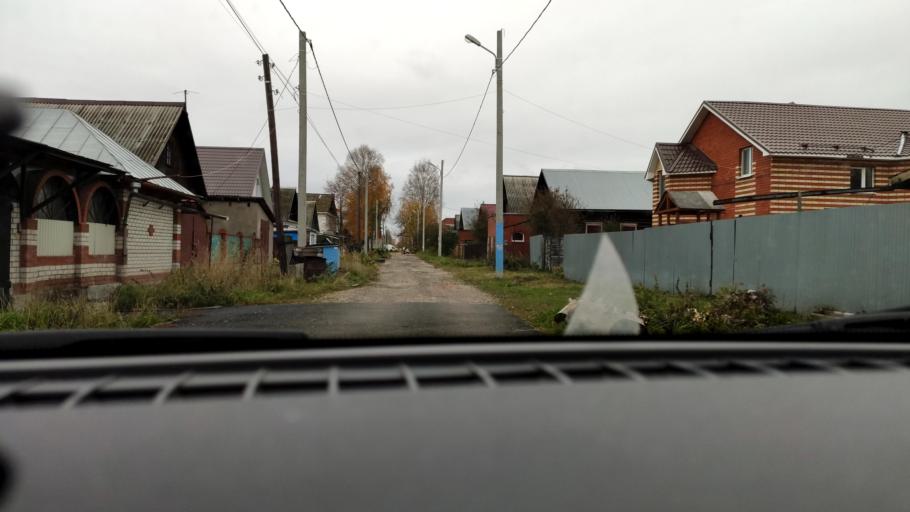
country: RU
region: Perm
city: Perm
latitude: 57.9795
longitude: 56.3036
